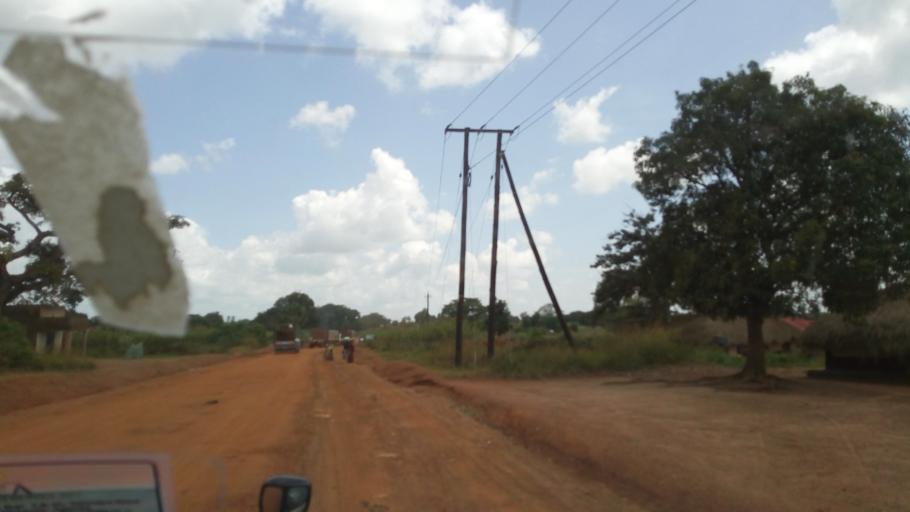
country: UG
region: Northern Region
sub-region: Yumbe District
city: Yumbe
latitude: 3.4736
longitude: 31.2539
